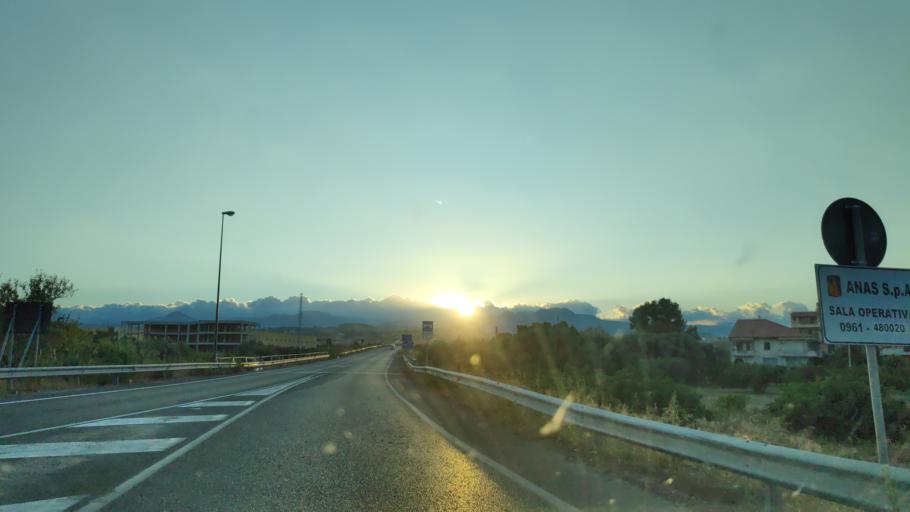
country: IT
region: Calabria
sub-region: Provincia di Reggio Calabria
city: Marina di Gioiosa Ionica
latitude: 38.2930
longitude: 16.3192
